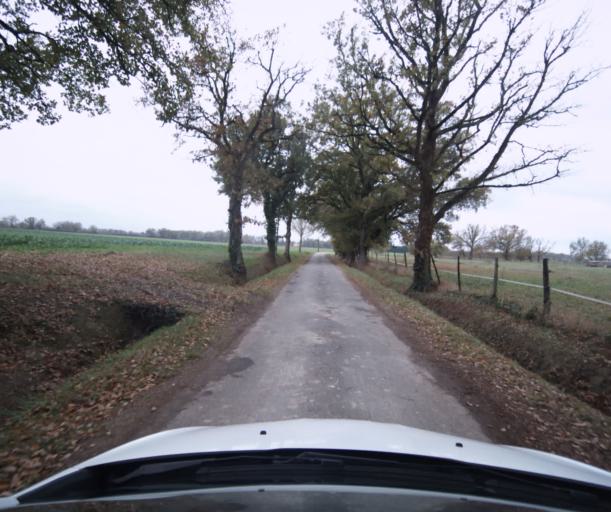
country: FR
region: Midi-Pyrenees
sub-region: Departement du Tarn-et-Garonne
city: Saint-Porquier
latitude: 44.0532
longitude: 1.1702
